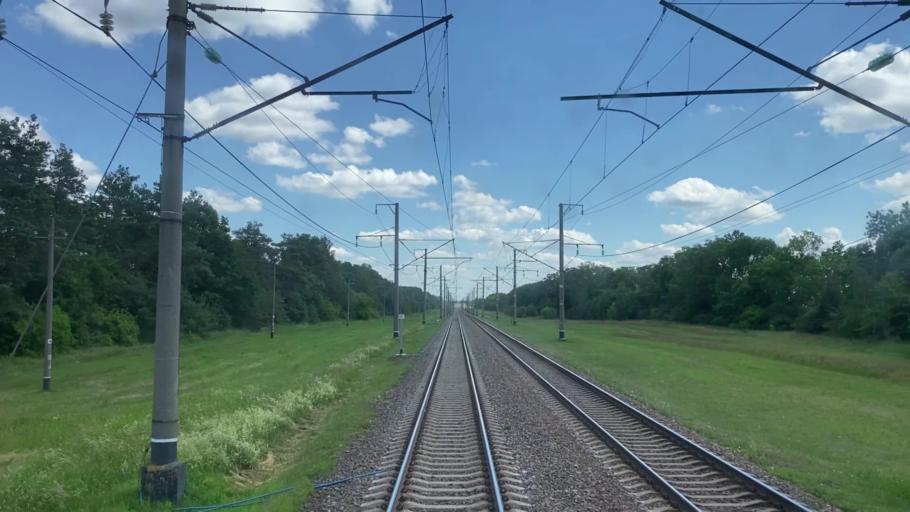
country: BY
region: Brest
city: Ivatsevichy
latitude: 52.8344
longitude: 25.5018
